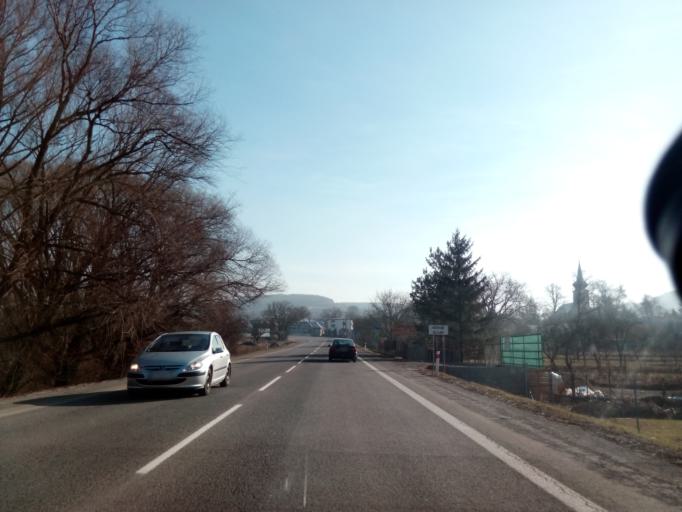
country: SK
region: Kosicky
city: Kosice
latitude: 48.7332
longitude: 21.3422
